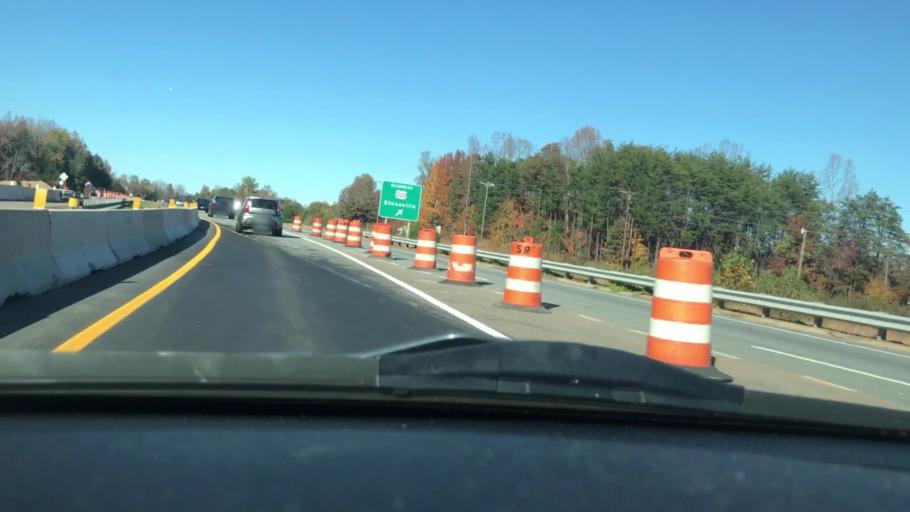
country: US
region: North Carolina
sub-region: Rockingham County
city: Stoneville
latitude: 36.4428
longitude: -79.9306
